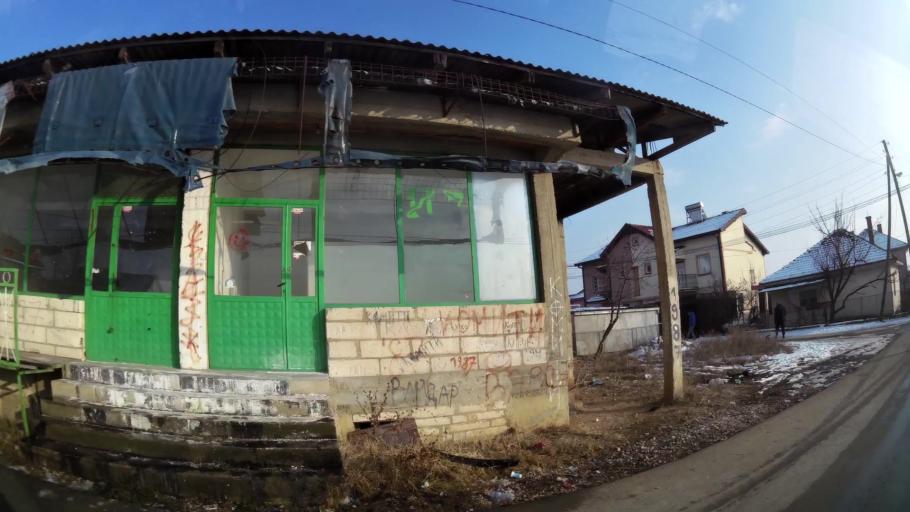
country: MK
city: Creshevo
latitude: 42.0318
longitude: 21.5177
